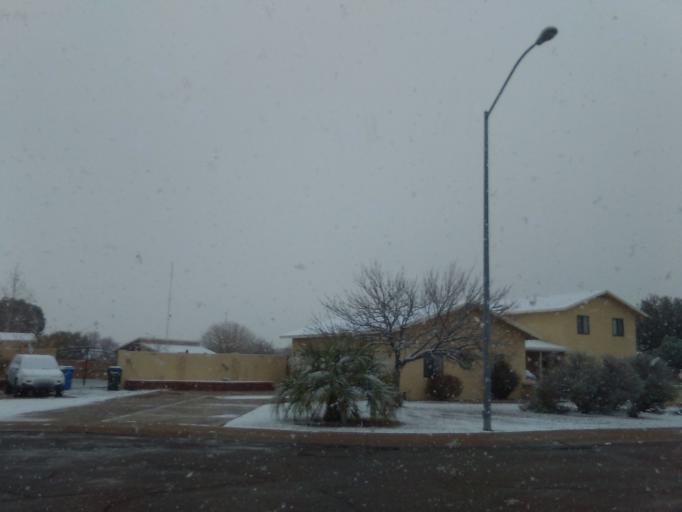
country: US
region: Arizona
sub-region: Cochise County
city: Sierra Vista
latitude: 31.5432
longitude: -110.2760
